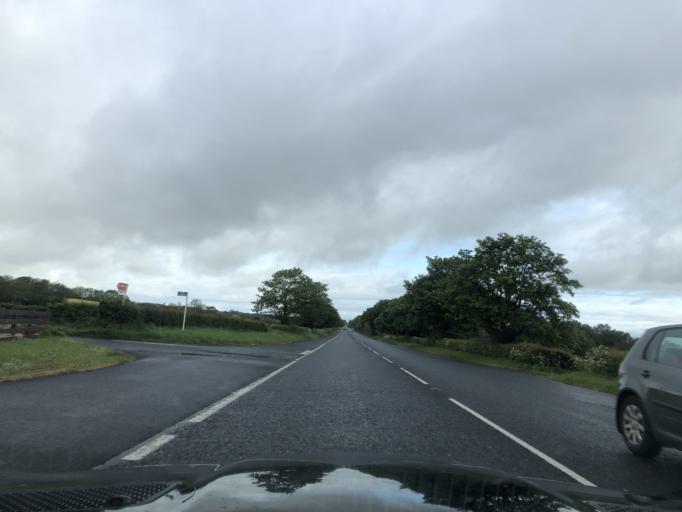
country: GB
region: Northern Ireland
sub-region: Ballymoney District
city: Ballymoney
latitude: 55.1050
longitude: -6.5407
